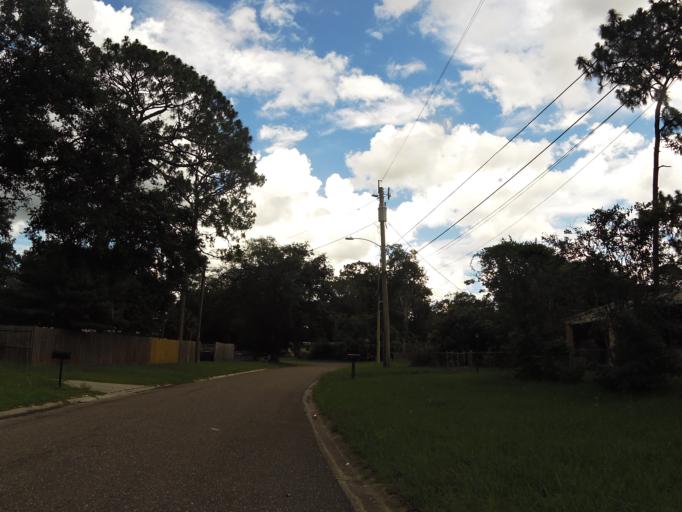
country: US
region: Florida
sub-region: Duval County
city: Jacksonville
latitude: 30.4241
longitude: -81.6685
